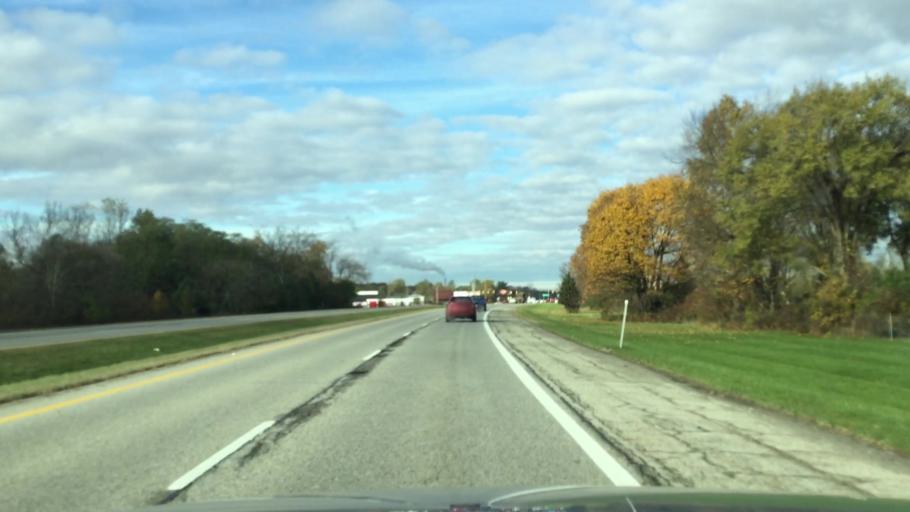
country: US
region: Michigan
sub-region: Kalamazoo County
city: Eastwood
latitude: 42.2694
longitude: -85.5255
